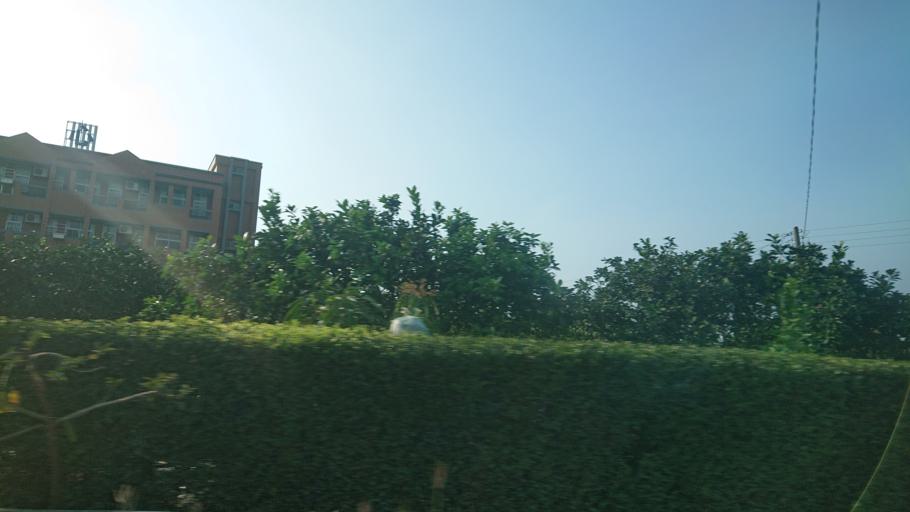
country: TW
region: Taiwan
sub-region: Tainan
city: Tainan
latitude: 23.1438
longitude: 120.2455
